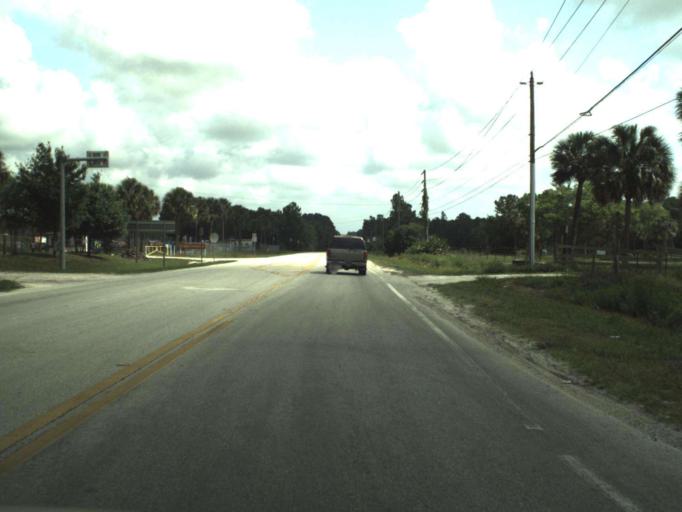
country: US
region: Florida
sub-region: Volusia County
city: Samsula-Spruce Creek
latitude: 29.0115
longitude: -81.0688
